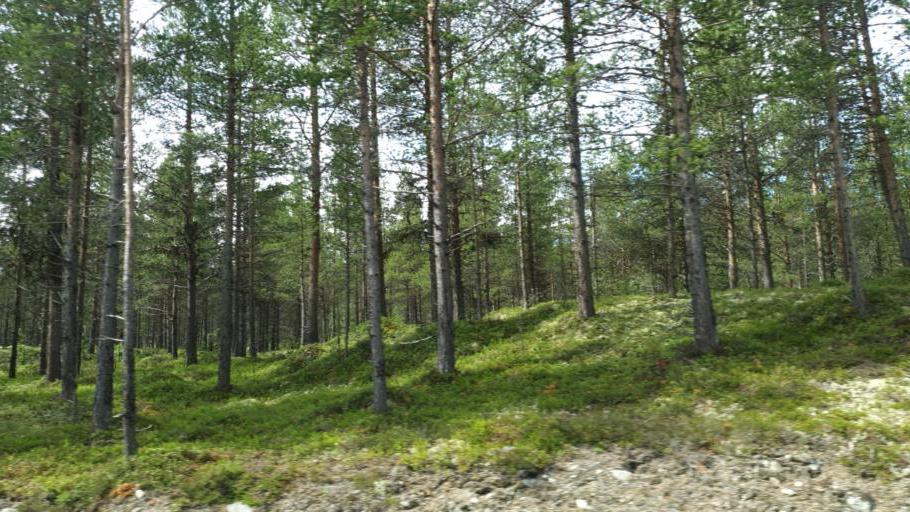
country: NO
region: Oppland
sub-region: Vaga
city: Vagamo
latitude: 61.6971
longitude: 9.0600
